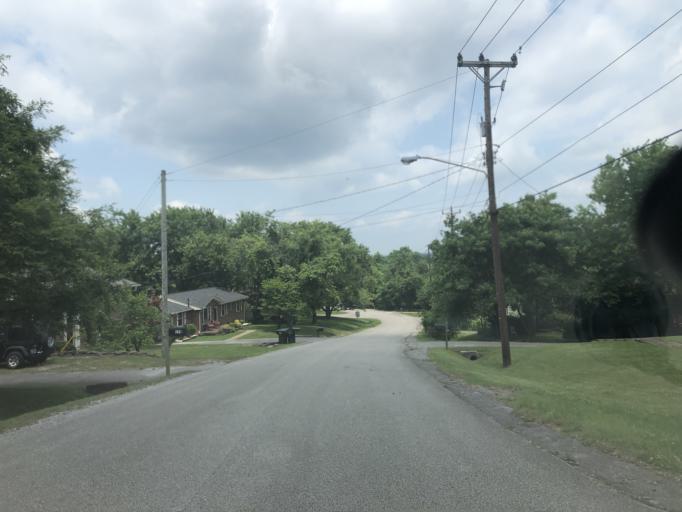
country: US
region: Tennessee
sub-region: Davidson County
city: Lakewood
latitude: 36.2070
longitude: -86.6294
